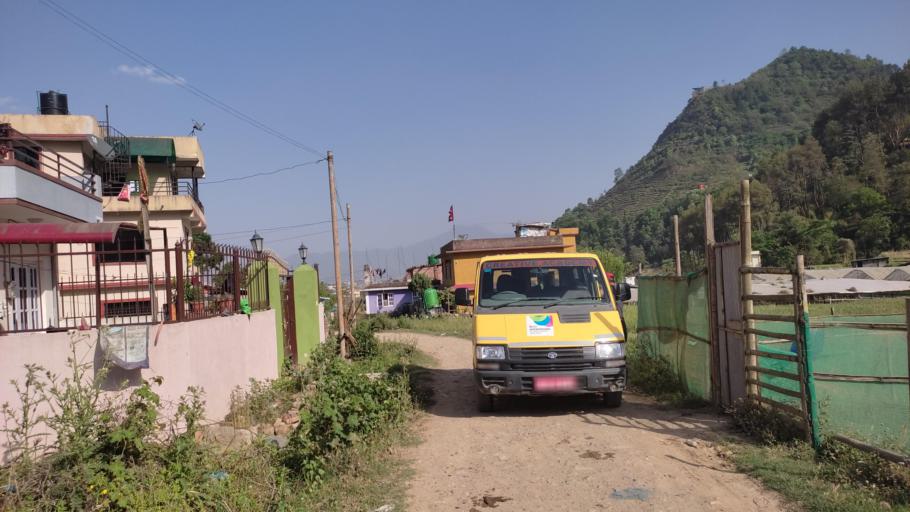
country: NP
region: Central Region
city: Kirtipur
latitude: 27.6605
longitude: 85.2625
